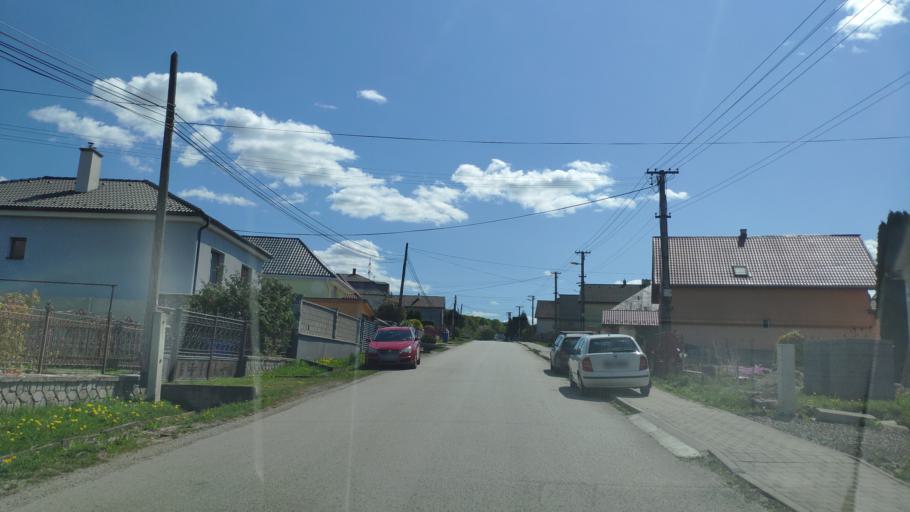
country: SK
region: Kosicky
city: Kosice
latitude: 48.6792
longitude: 21.4310
